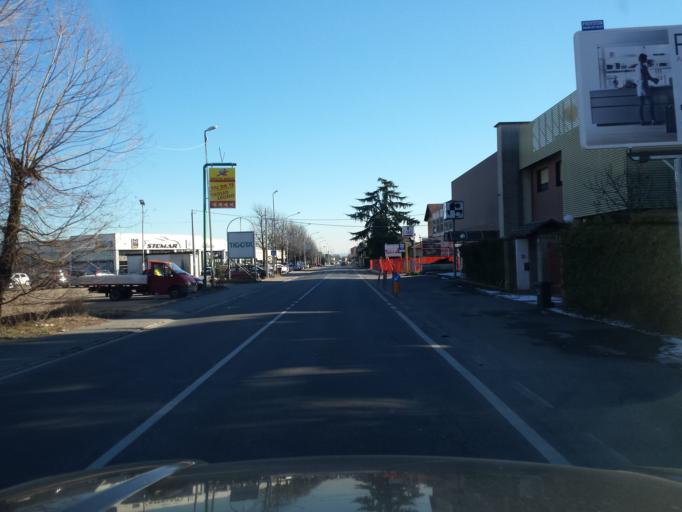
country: IT
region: Piedmont
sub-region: Provincia di Torino
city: Feletto
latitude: 45.3150
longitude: 7.7363
